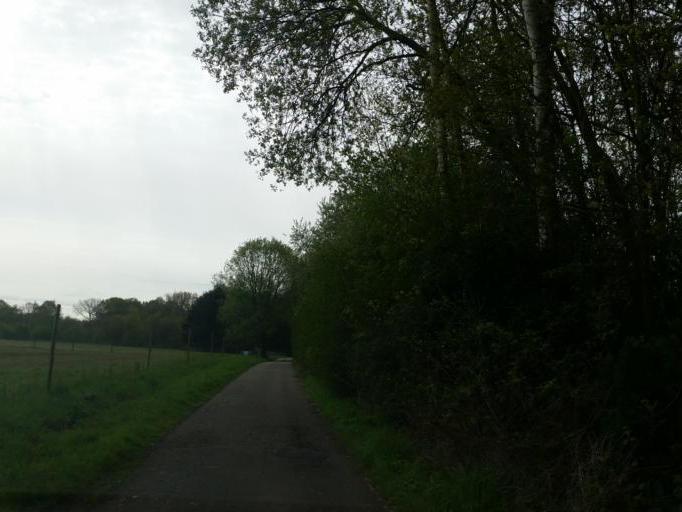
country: BE
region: Flanders
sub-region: Provincie Vlaams-Brabant
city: Kampenhout
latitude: 50.9746
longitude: 4.5329
